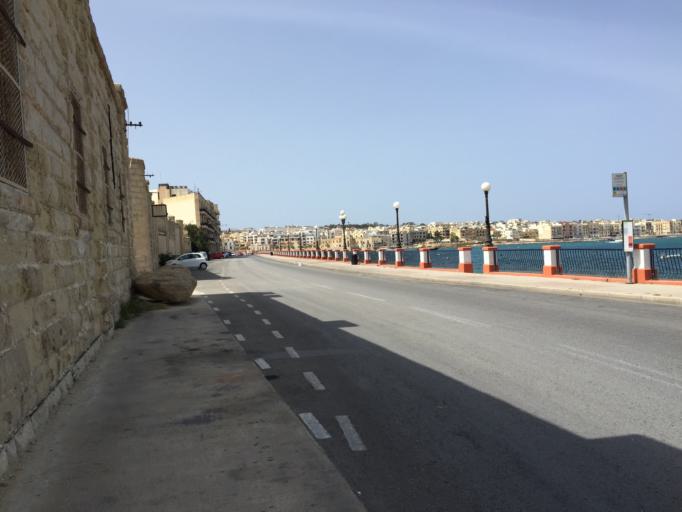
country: MT
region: Birzebbuga
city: Birzebbuga
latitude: 35.8273
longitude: 14.5332
